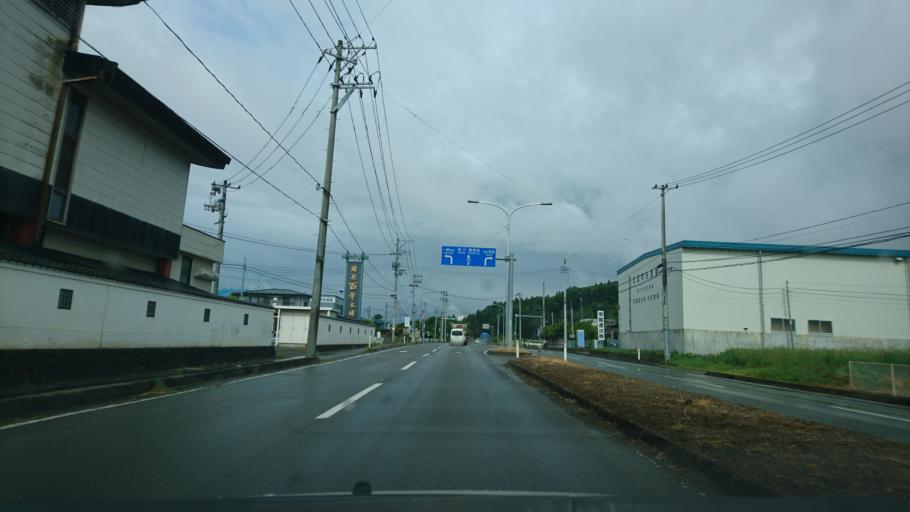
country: JP
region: Iwate
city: Ichinoseki
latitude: 38.9409
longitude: 141.0842
